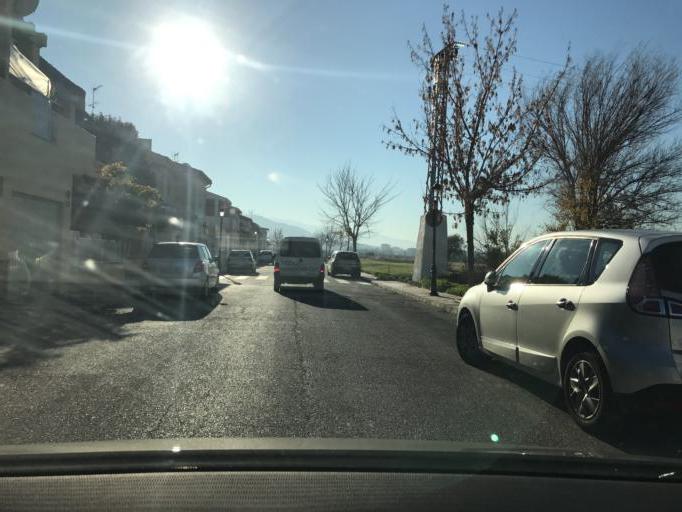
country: ES
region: Andalusia
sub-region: Provincia de Granada
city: Pulianas
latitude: 37.2172
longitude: -3.6062
